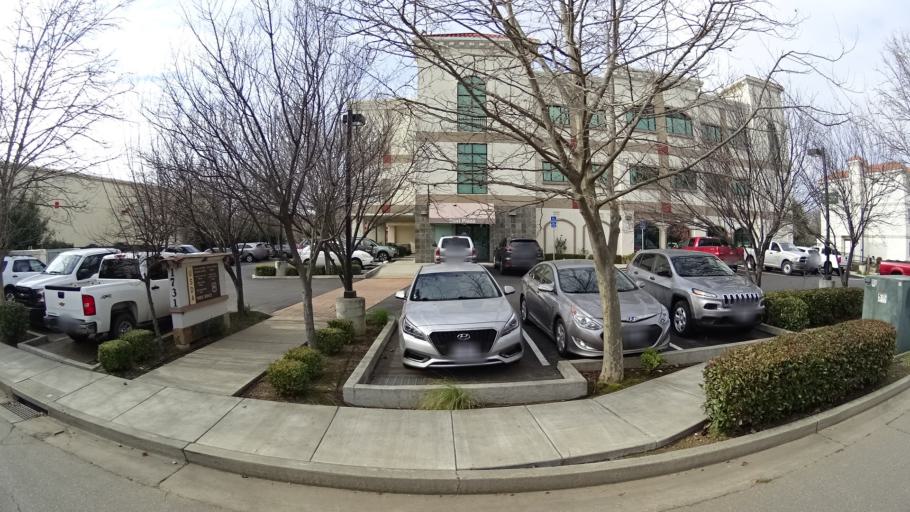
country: US
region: California
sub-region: Yolo County
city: Davis
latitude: 38.5416
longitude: -121.7315
